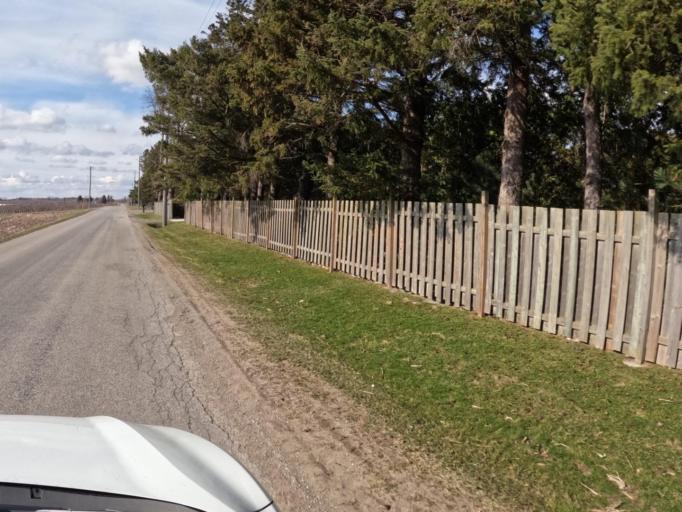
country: CA
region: Ontario
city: Norfolk County
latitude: 42.8684
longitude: -80.2769
